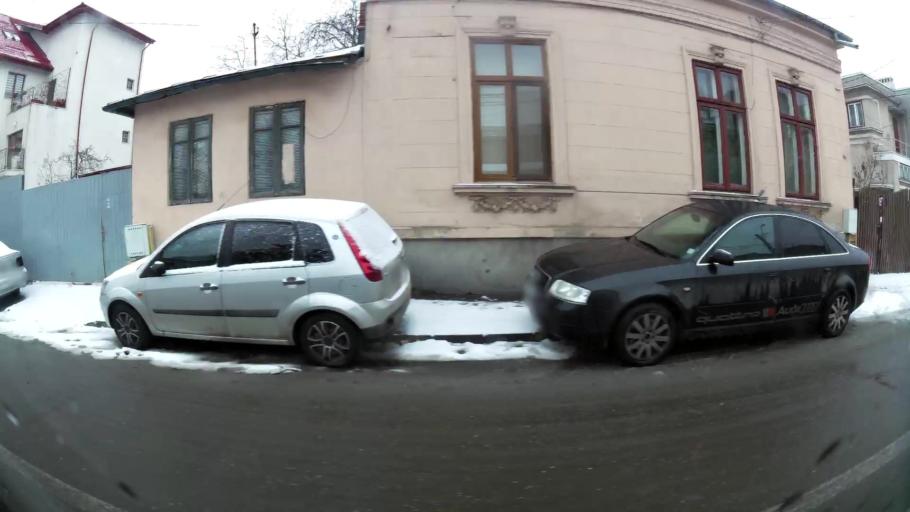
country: RO
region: Prahova
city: Ploiesti
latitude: 44.9356
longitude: 26.0202
